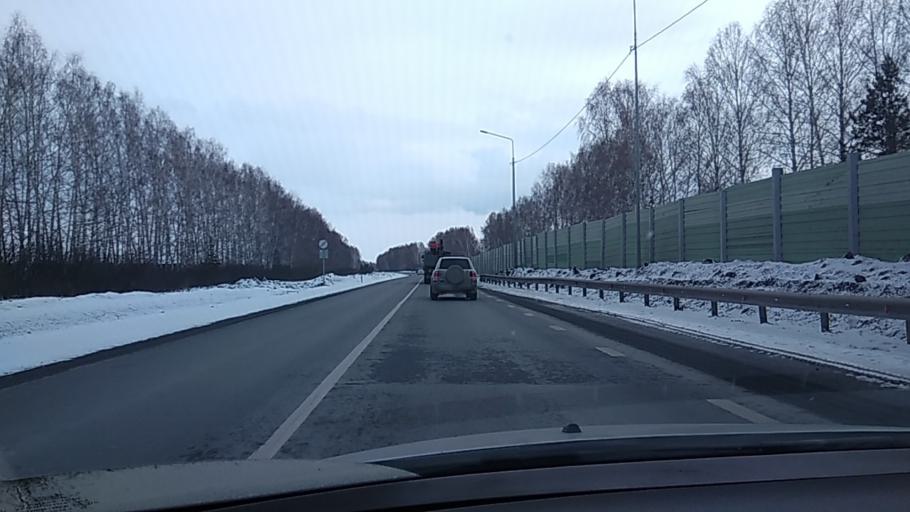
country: RU
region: Sverdlovsk
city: Sovkhoznyy
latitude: 56.5179
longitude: 61.4425
